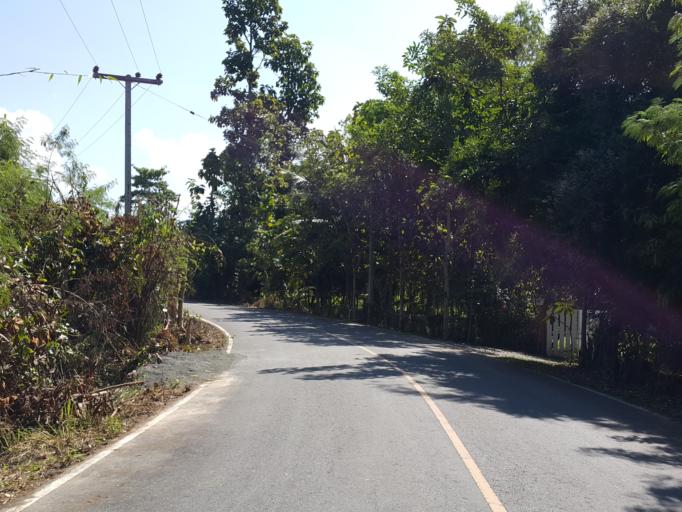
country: TH
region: Chiang Mai
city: Mae On
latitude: 18.8625
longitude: 99.1645
